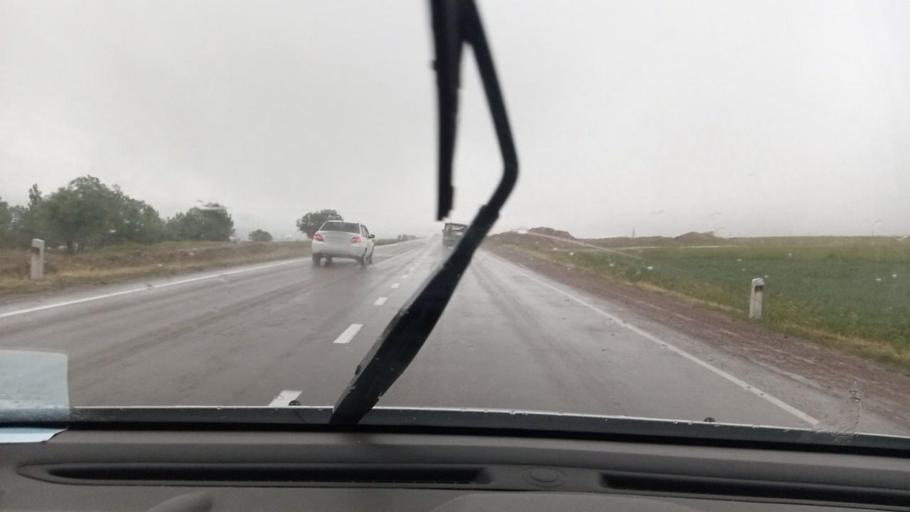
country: UZ
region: Toshkent
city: Angren
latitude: 41.0422
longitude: 70.1489
